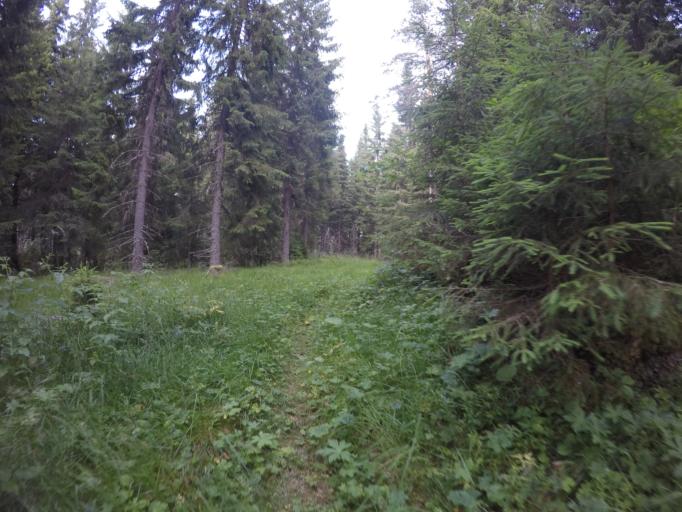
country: SE
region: Vaermland
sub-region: Filipstads Kommun
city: Lesjofors
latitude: 60.2038
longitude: 14.2994
